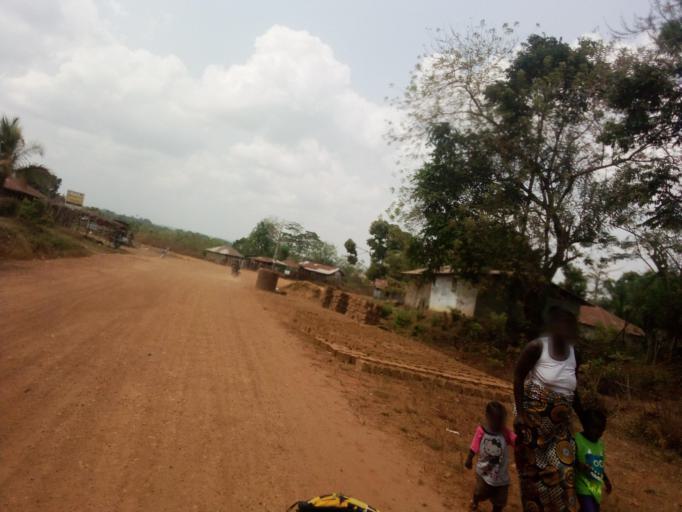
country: SL
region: Southern Province
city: Mogbwemo
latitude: 7.6645
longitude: -12.2764
